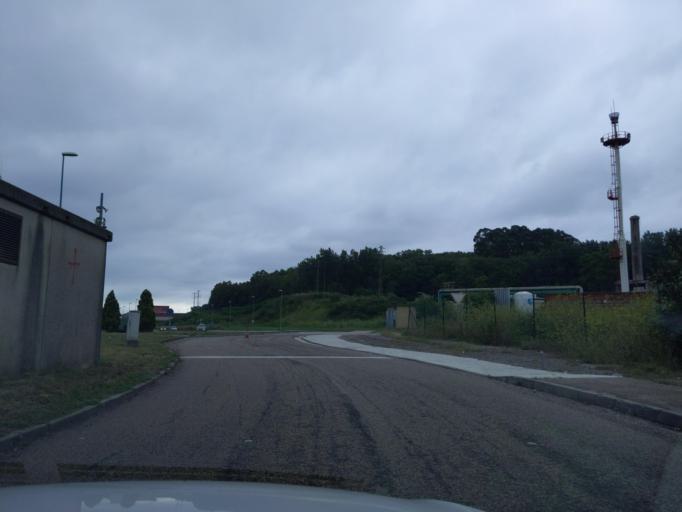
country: ES
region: Asturias
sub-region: Province of Asturias
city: Aviles
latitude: 43.5600
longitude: -5.8948
